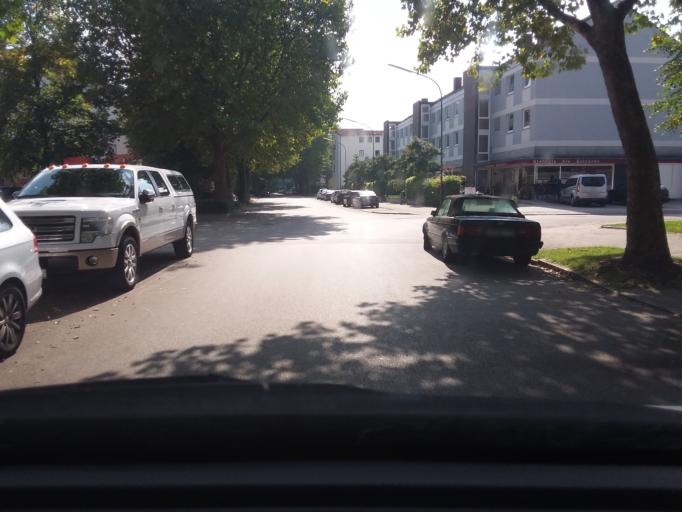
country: DE
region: Bavaria
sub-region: Upper Bavaria
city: Dachau
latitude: 48.2634
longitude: 11.4572
